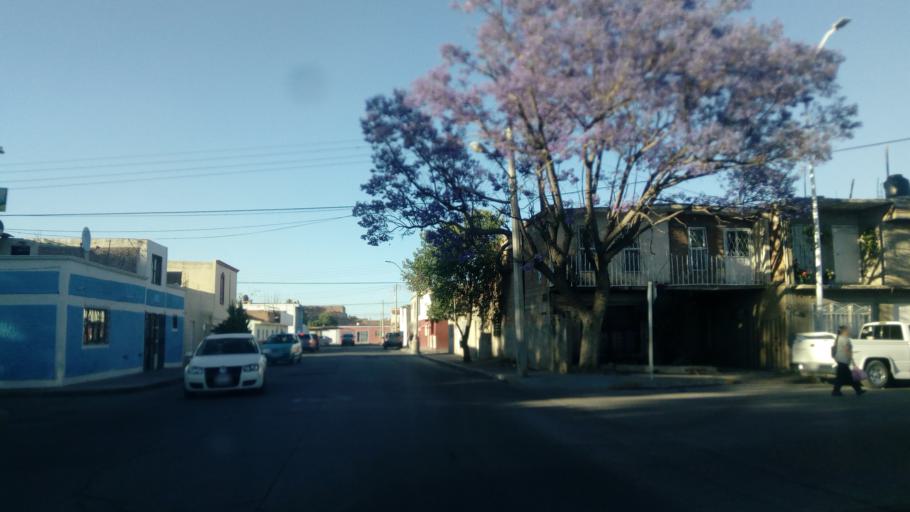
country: MX
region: Durango
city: Victoria de Durango
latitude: 24.0006
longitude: -104.6745
